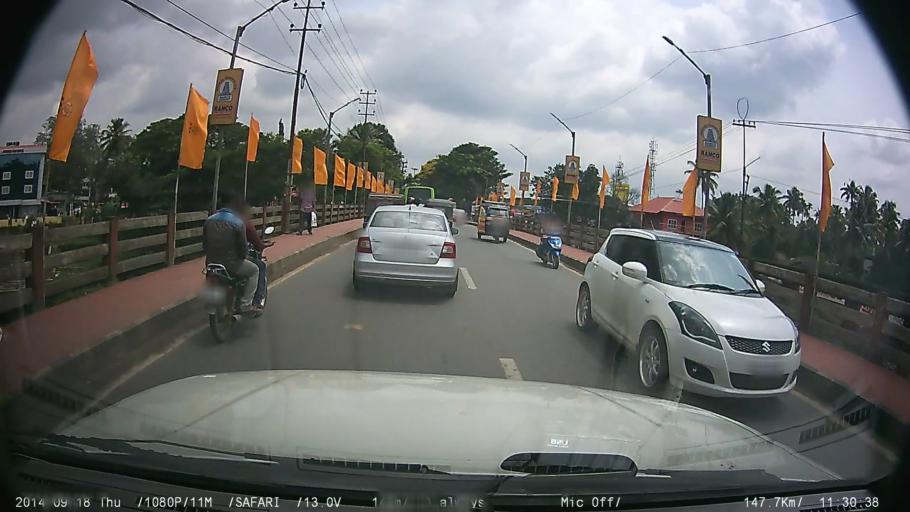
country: IN
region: Kerala
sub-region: Ernakulam
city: Muvattupula
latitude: 9.9878
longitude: 76.5780
